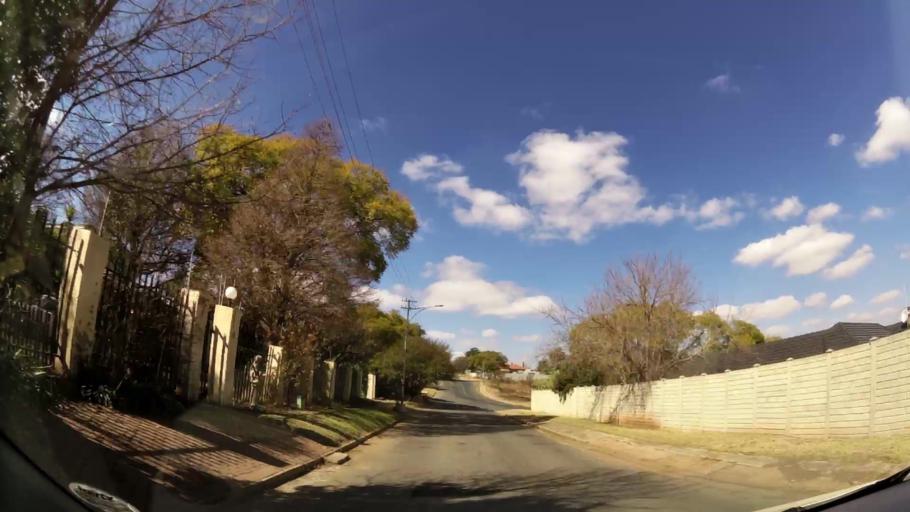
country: ZA
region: Gauteng
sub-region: West Rand District Municipality
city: Krugersdorp
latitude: -26.0958
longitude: 27.7850
